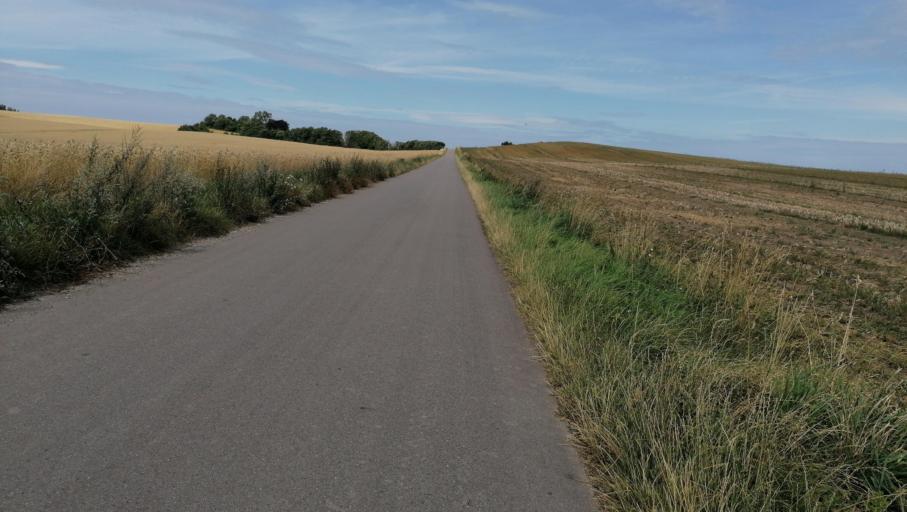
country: DK
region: Zealand
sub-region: Odsherred Kommune
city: Horve
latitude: 55.7600
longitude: 11.4546
